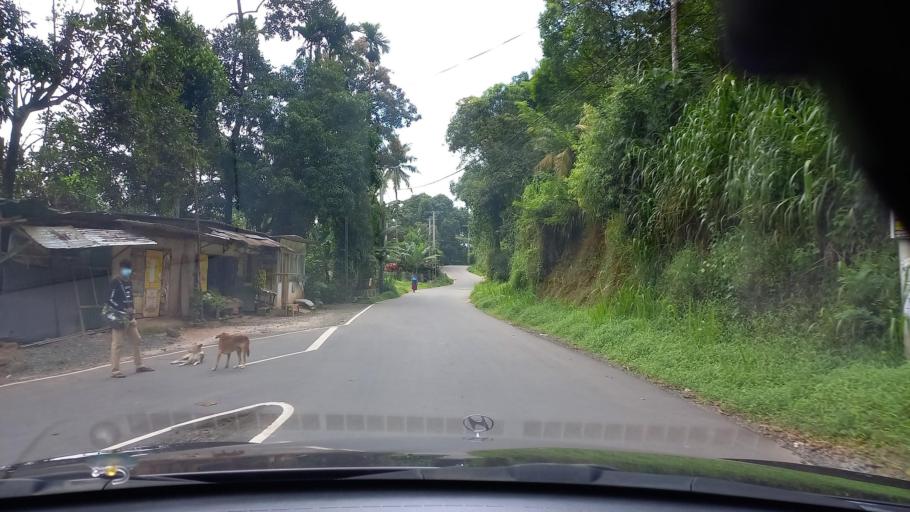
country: LK
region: Central
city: Gampola
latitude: 7.2127
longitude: 80.6152
